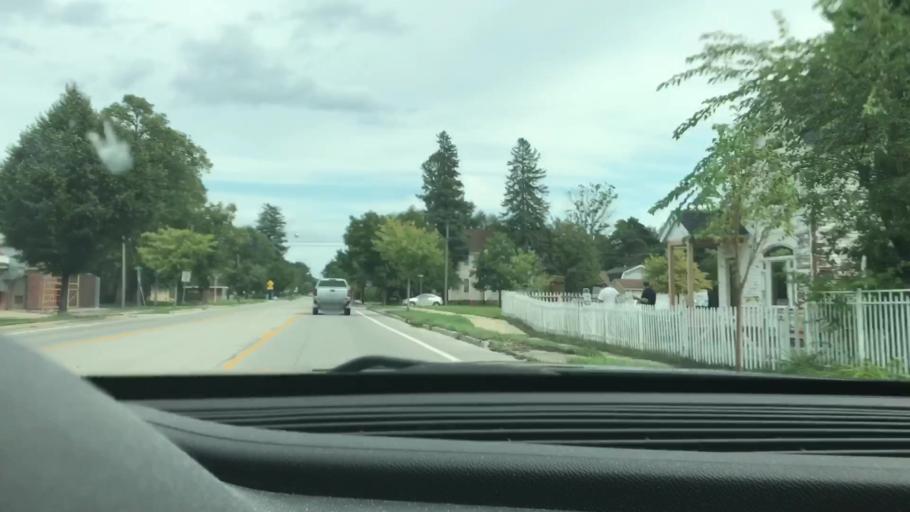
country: US
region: Michigan
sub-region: Antrim County
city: Bellaire
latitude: 44.9757
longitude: -85.2078
